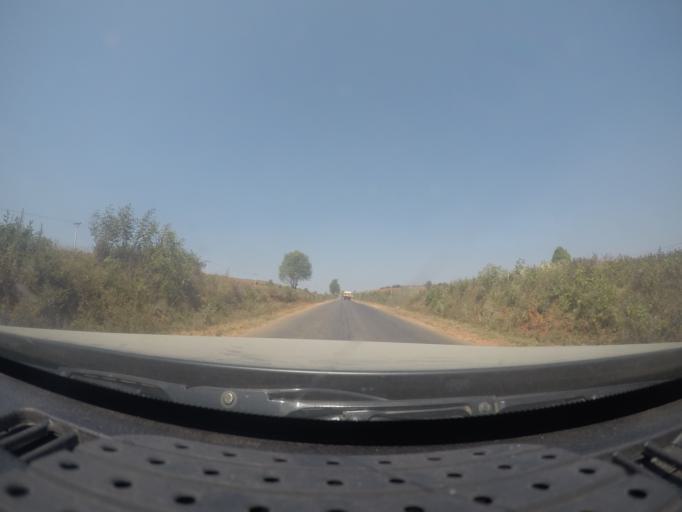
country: MM
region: Shan
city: Taunggyi
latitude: 20.8094
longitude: 96.6177
